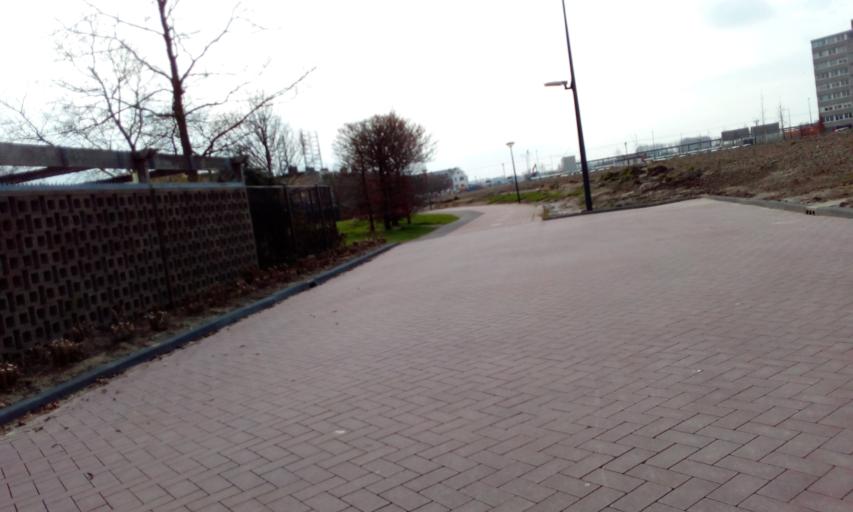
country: NL
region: South Holland
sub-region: Gemeente Maassluis
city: Maassluis
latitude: 51.9275
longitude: 4.2382
